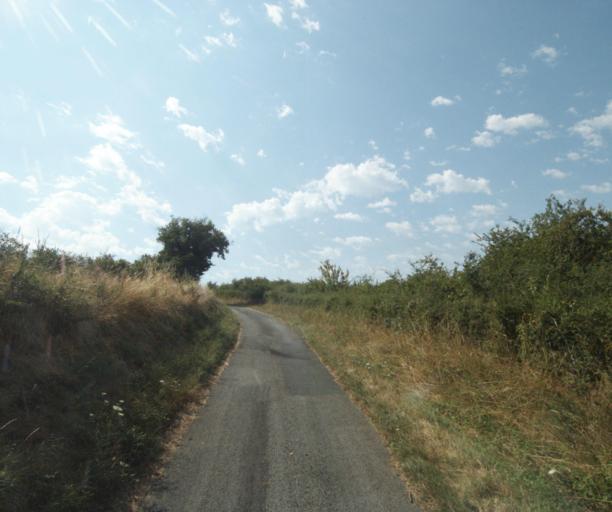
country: FR
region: Rhone-Alpes
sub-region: Departement du Rhone
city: Lentilly
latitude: 45.8438
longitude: 4.6477
